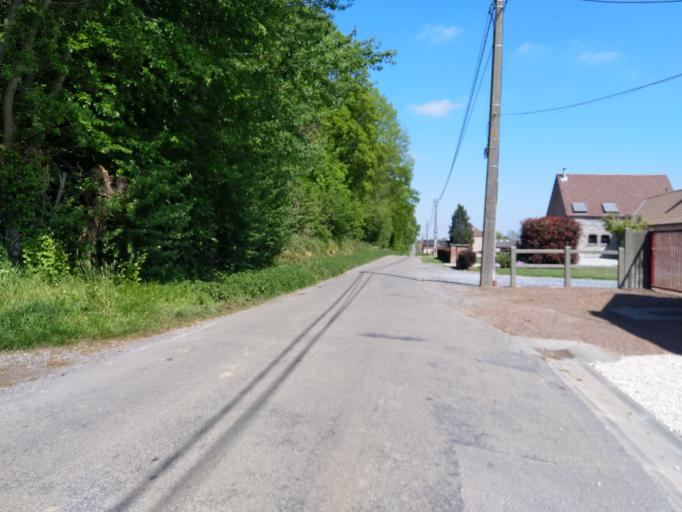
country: BE
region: Wallonia
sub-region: Province du Hainaut
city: Brugelette
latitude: 50.5463
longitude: 3.8434
